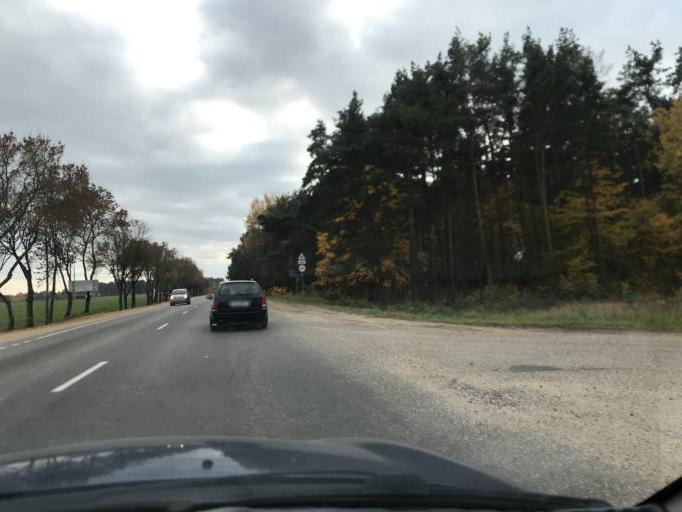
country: BY
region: Grodnenskaya
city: Lida
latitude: 53.8776
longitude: 25.2576
